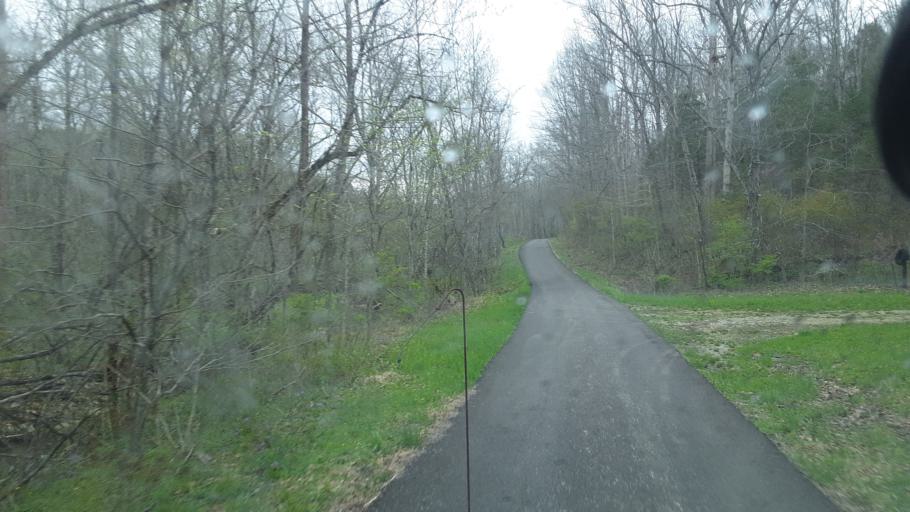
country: US
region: Kentucky
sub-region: Owen County
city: Owenton
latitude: 38.6542
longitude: -84.7867
